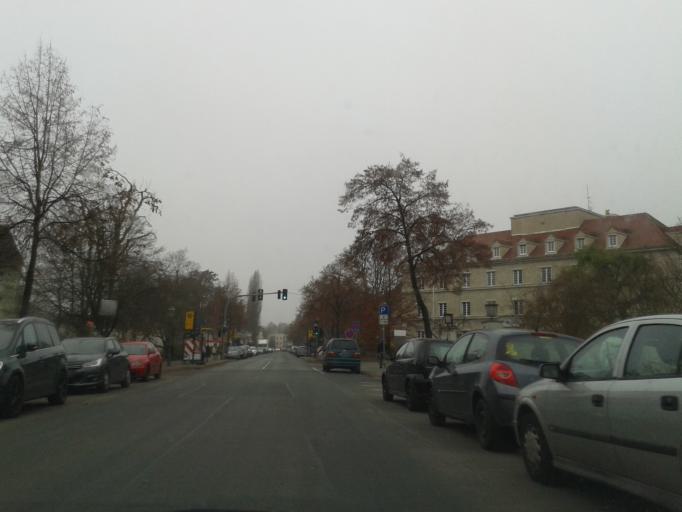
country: DE
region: Saxony
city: Dresden
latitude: 51.0895
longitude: 13.7098
